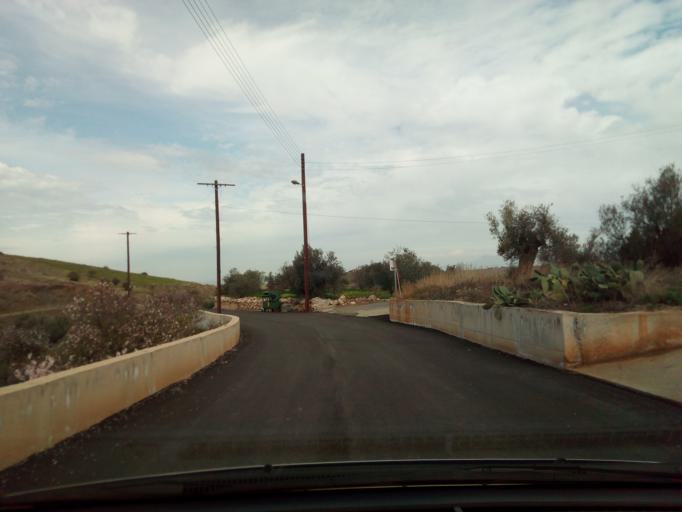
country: CY
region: Lefkosia
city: Astromeritis
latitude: 35.0763
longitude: 32.9944
